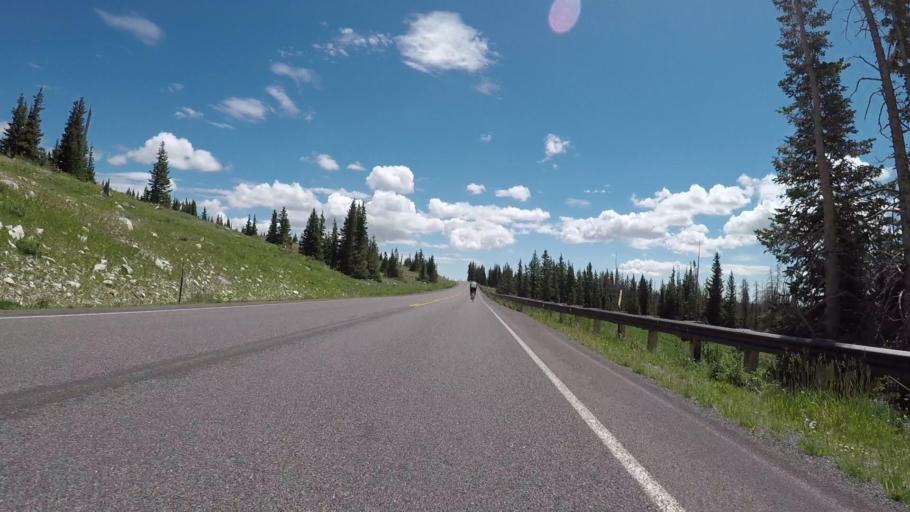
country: US
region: Wyoming
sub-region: Carbon County
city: Saratoga
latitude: 41.3511
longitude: -106.2782
